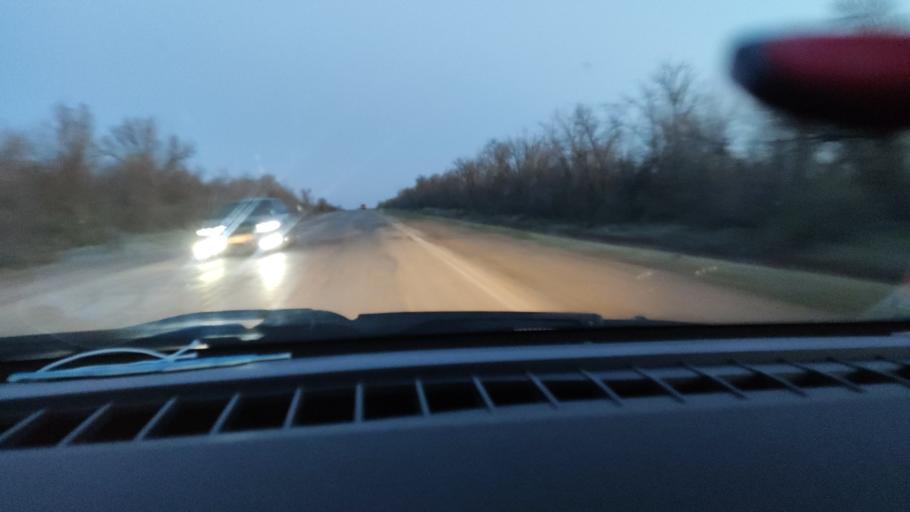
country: RU
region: Saratov
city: Rovnoye
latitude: 50.9945
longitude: 46.1078
